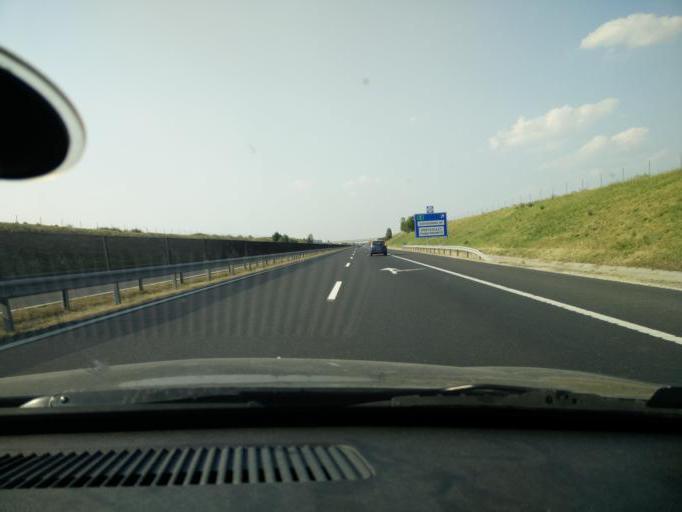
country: HU
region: Fejer
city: Rackeresztur
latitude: 47.2988
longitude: 18.8659
